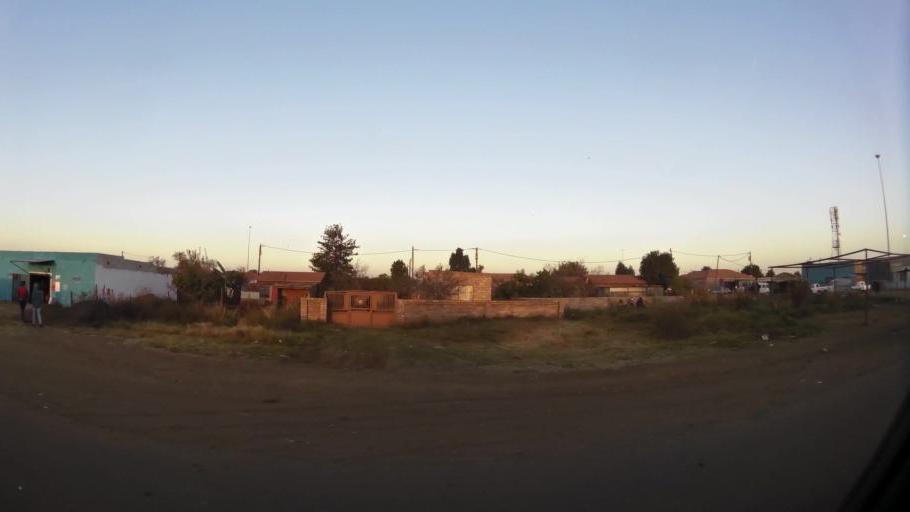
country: ZA
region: North-West
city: Ga-Rankuwa
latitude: -25.5849
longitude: 28.0462
